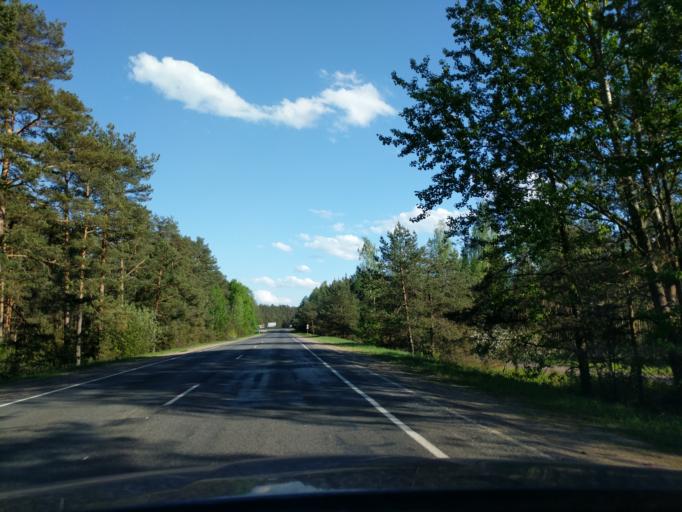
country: BY
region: Minsk
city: Myadzyel
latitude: 54.8356
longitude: 26.9355
